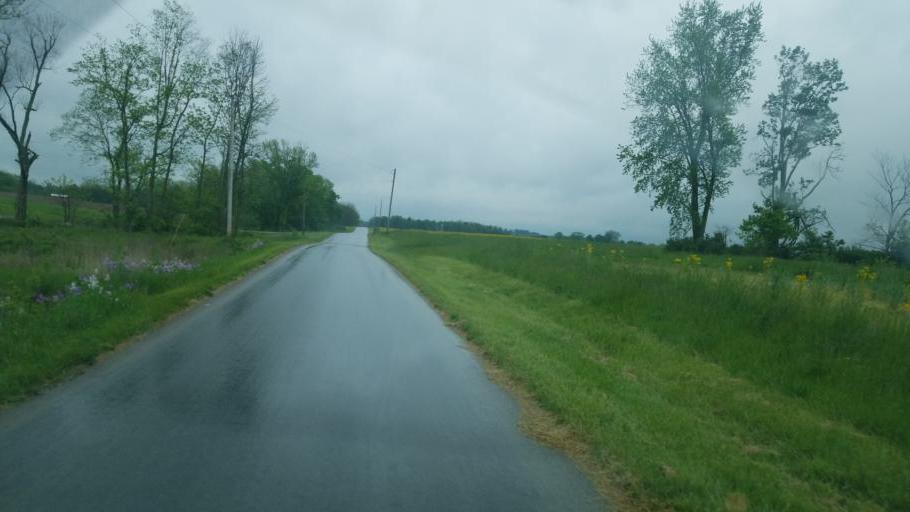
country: US
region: Ohio
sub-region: Highland County
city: Greenfield
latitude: 39.3265
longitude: -83.4272
